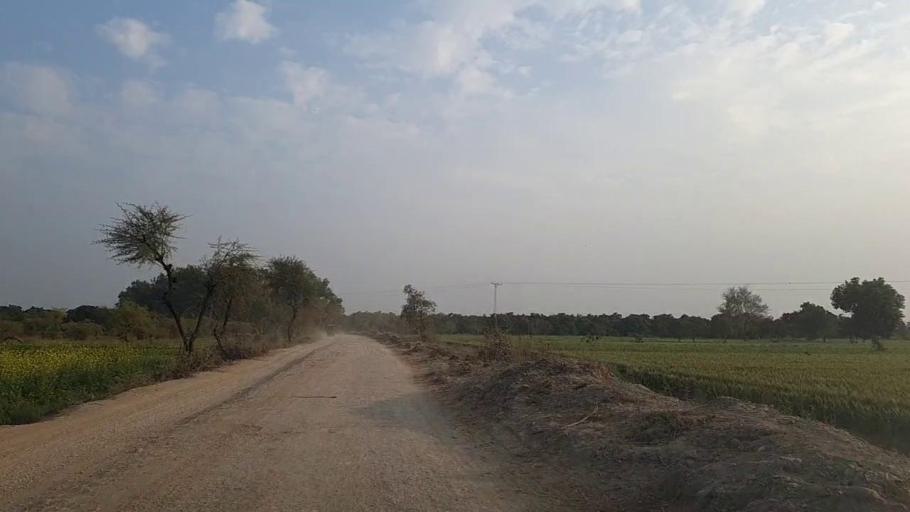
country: PK
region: Sindh
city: Mirwah Gorchani
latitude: 25.3082
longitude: 69.2116
